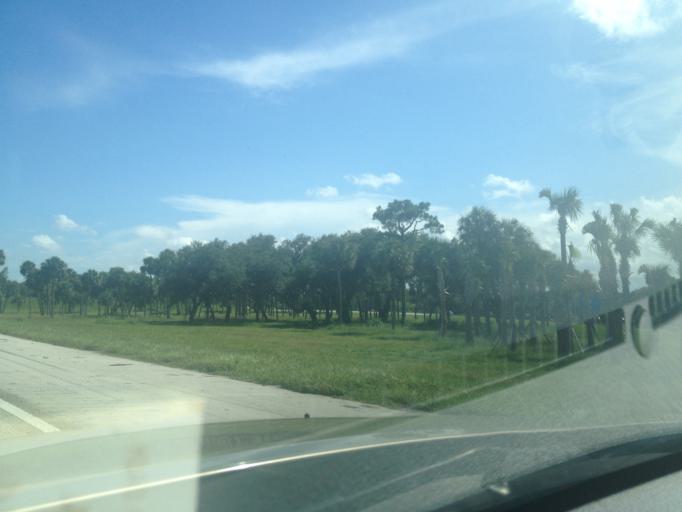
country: US
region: Florida
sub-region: Broward County
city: Deerfield Beach
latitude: 26.3219
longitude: -80.1167
